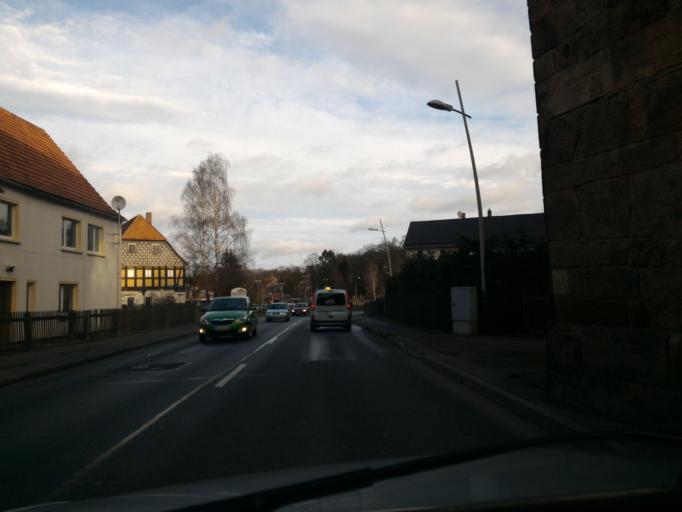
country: DE
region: Saxony
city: Ebersbach
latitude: 51.0113
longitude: 14.5816
